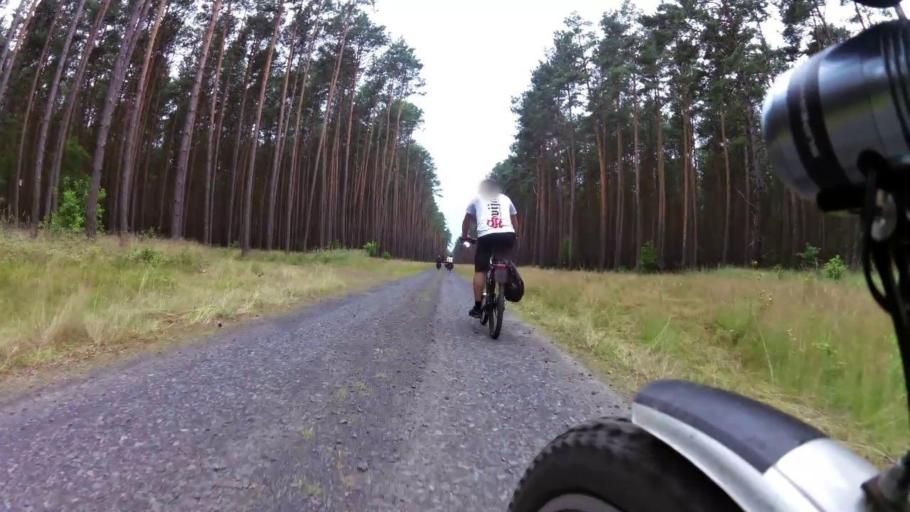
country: PL
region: West Pomeranian Voivodeship
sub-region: Powiat mysliborski
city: Debno
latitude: 52.8313
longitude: 14.6263
